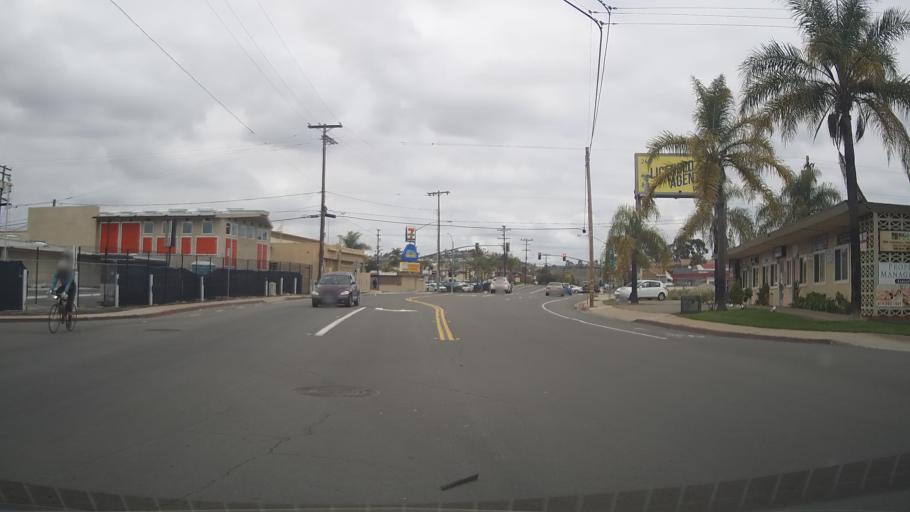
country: US
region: California
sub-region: San Diego County
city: La Mesa
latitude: 32.7674
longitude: -117.0473
